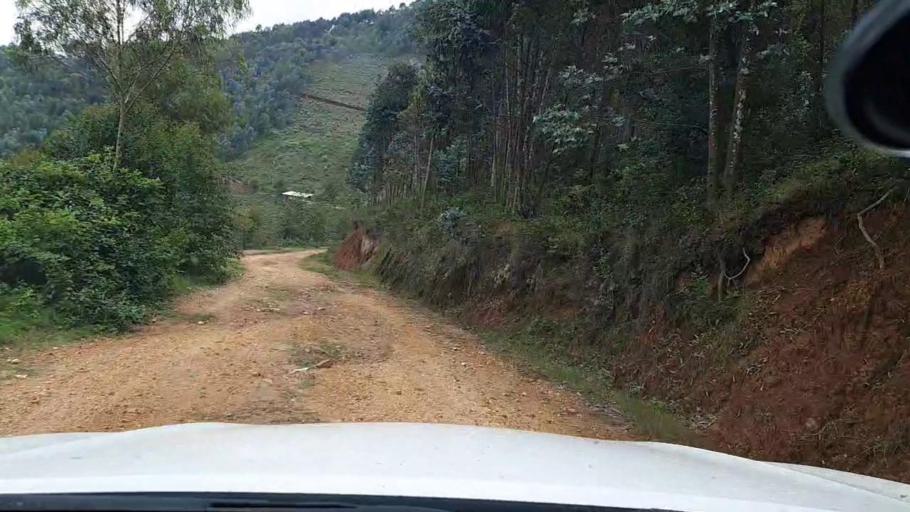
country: RW
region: Western Province
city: Kibuye
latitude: -2.1611
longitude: 29.4541
